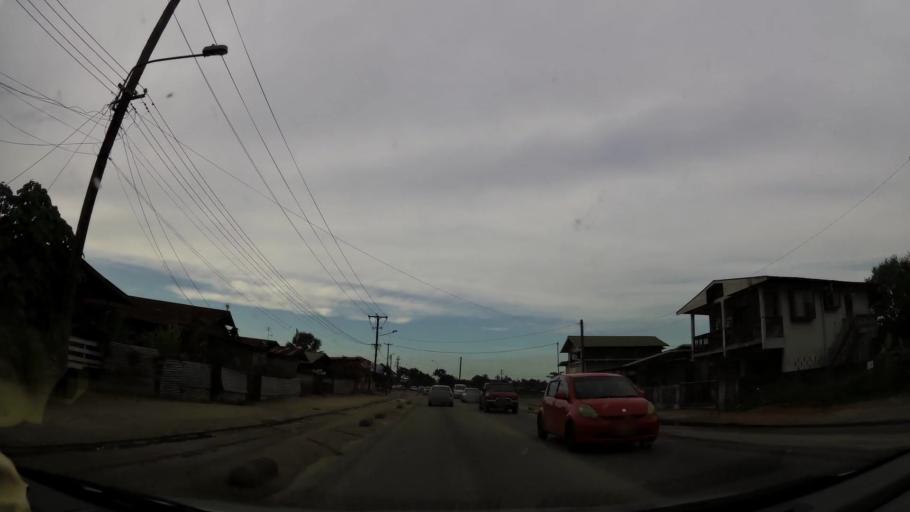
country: SR
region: Paramaribo
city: Paramaribo
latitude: 5.7983
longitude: -55.1891
